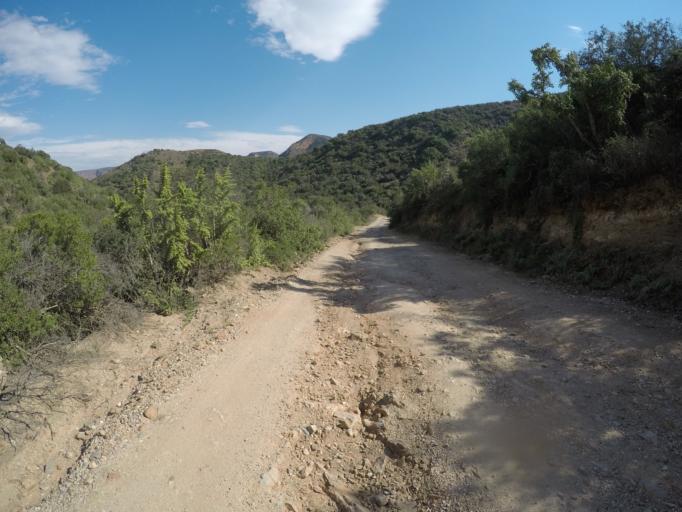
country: ZA
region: Eastern Cape
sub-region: Cacadu District Municipality
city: Kareedouw
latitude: -33.6548
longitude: 24.4040
